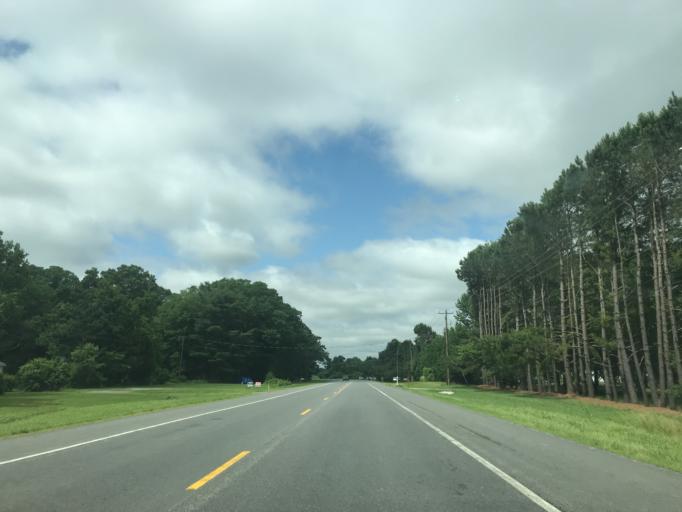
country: US
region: Maryland
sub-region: Caroline County
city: Ridgely
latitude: 38.9255
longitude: -75.9287
